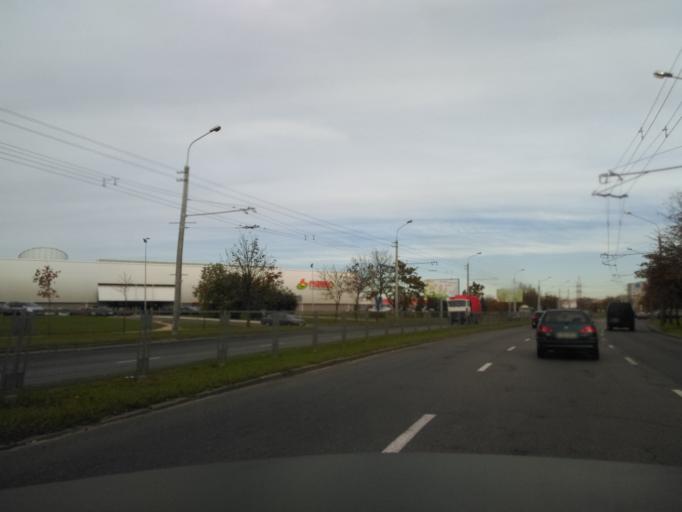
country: BY
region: Minsk
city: Minsk
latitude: 53.8738
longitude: 27.5971
